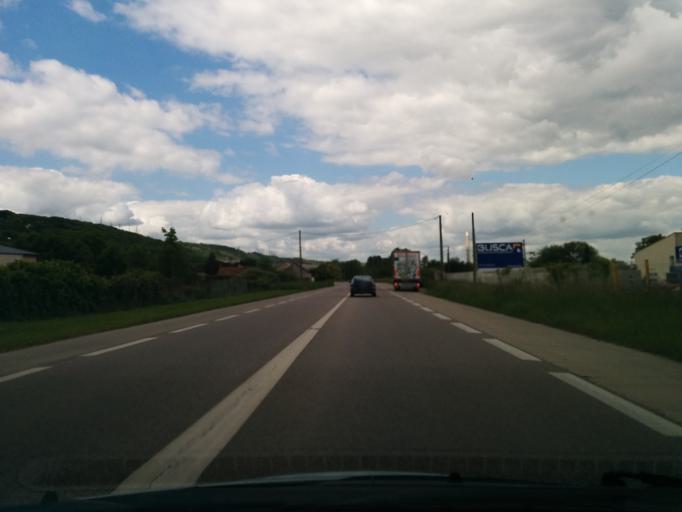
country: FR
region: Ile-de-France
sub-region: Departement des Yvelines
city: Mezieres-sur-Seine
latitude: 48.9624
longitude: 1.7960
